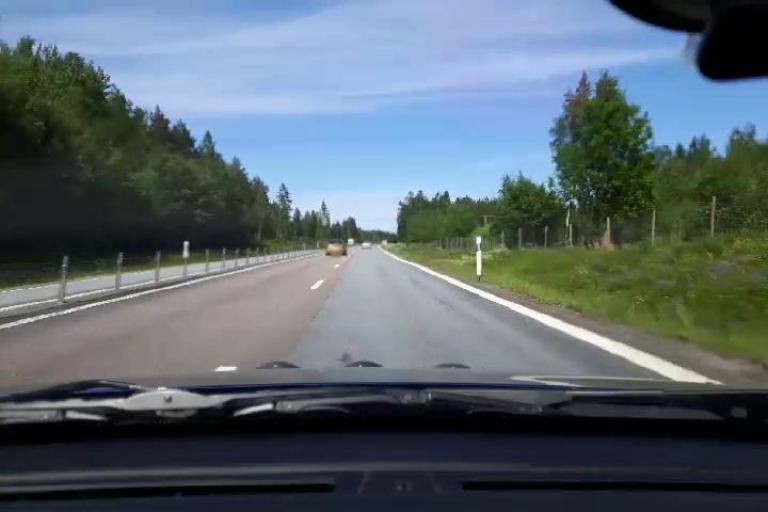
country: SE
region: Gaevleborg
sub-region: Gavle Kommun
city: Norrsundet
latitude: 60.9353
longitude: 17.0139
